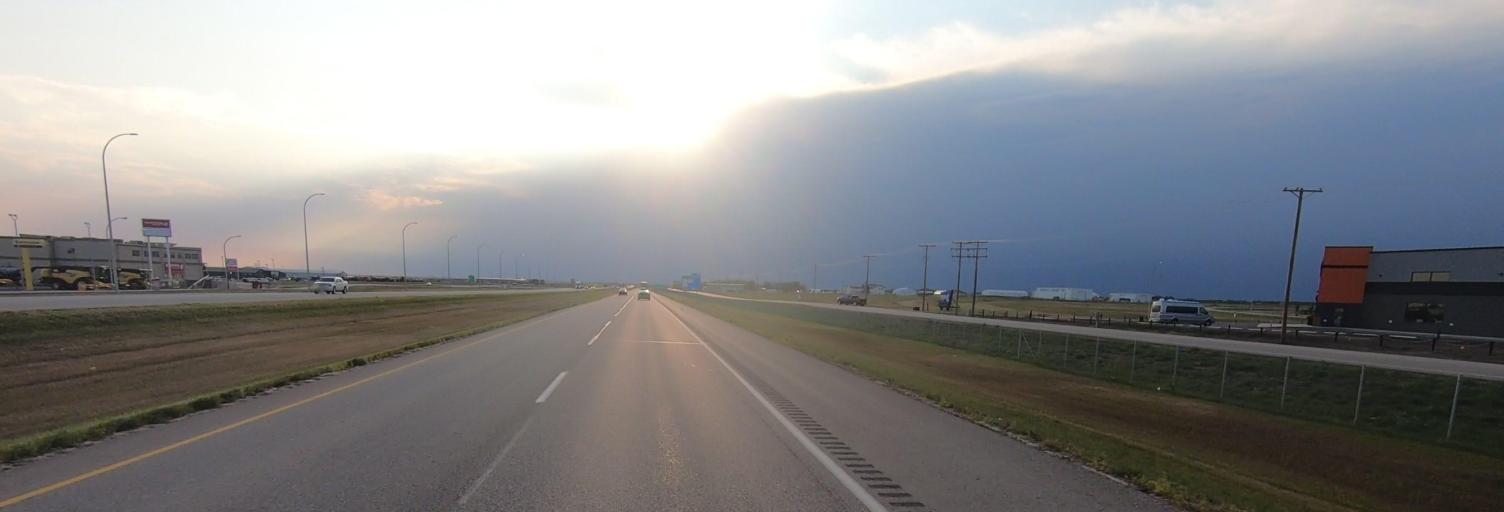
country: CA
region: Saskatchewan
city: Pilot Butte
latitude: 50.4514
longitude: -104.4027
